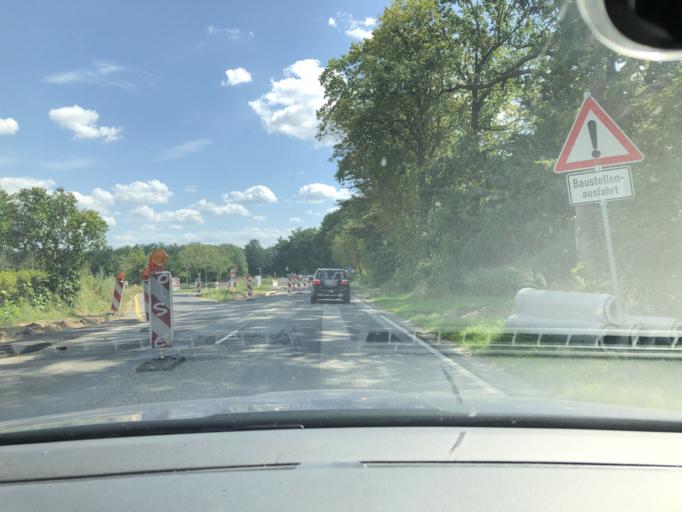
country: DE
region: Brandenburg
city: Neuruppin
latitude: 52.9278
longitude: 12.8981
